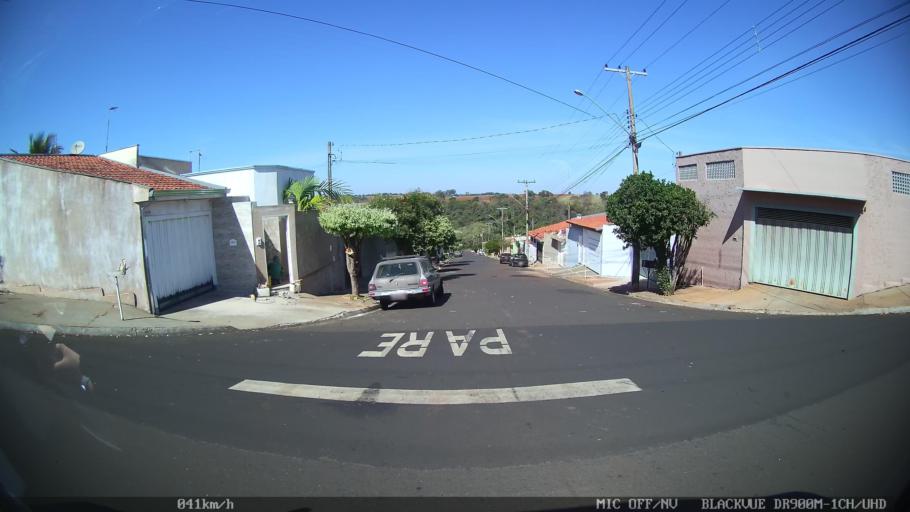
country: BR
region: Sao Paulo
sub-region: Batatais
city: Batatais
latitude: -20.8888
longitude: -47.5682
